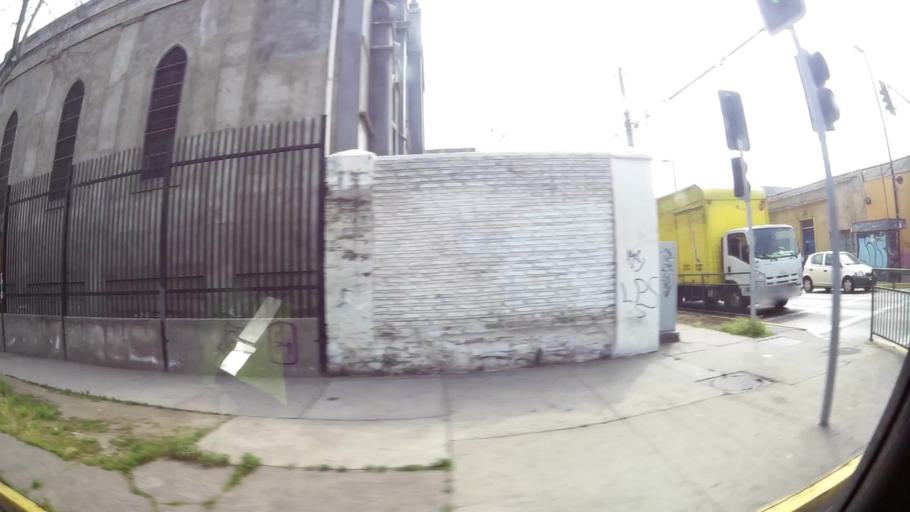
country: CL
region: Santiago Metropolitan
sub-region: Provincia de Santiago
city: Santiago
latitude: -33.4693
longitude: -70.6440
